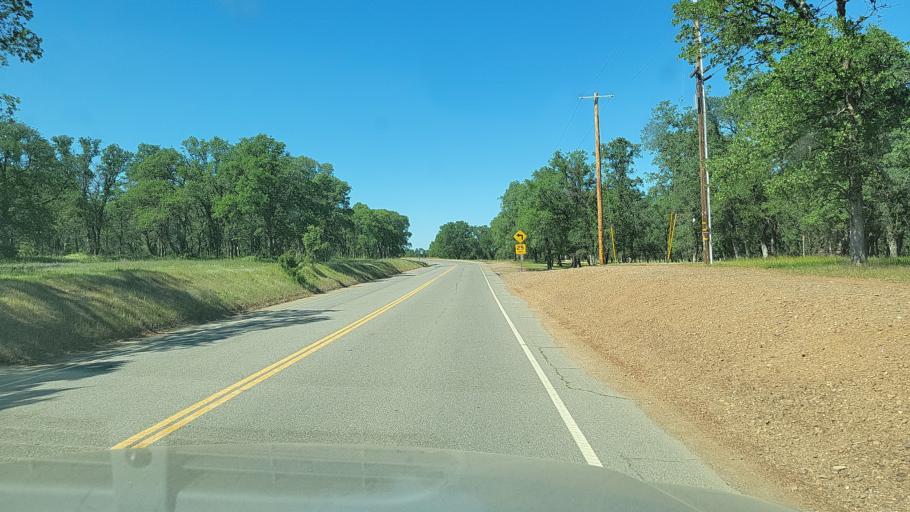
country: US
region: California
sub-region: Tehama County
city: Red Bluff
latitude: 40.2181
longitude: -122.2486
